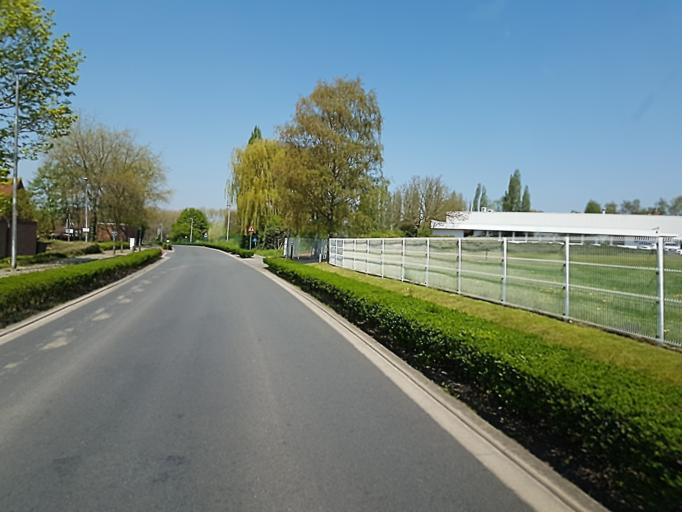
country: BE
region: Flanders
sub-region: Provincie West-Vlaanderen
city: Kortrijk
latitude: 50.8078
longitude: 3.2439
